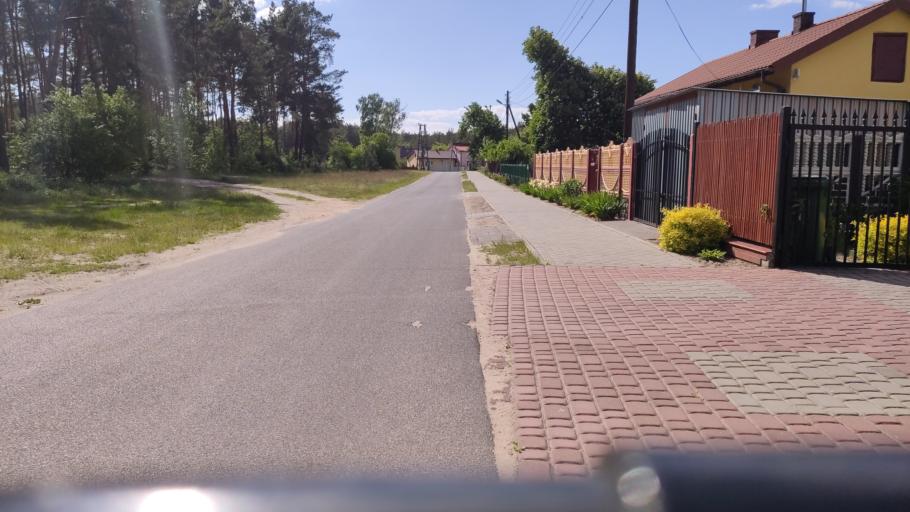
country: PL
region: Kujawsko-Pomorskie
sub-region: Wloclawek
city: Wloclawek
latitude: 52.6034
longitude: 19.0795
